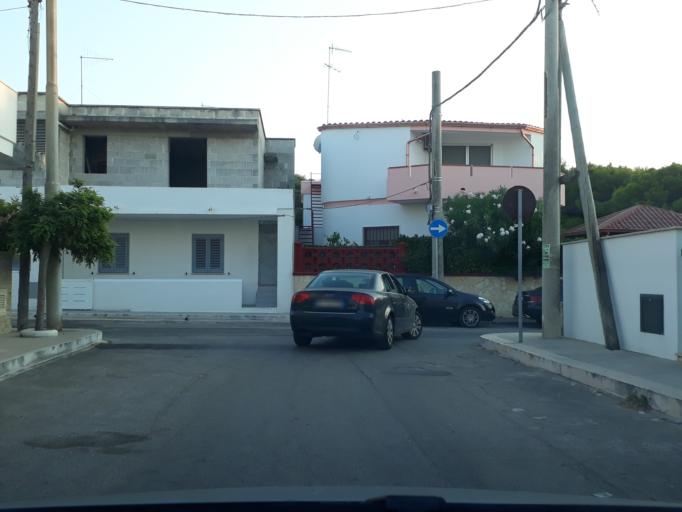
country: IT
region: Apulia
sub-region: Provincia di Brindisi
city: Carovigno
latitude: 40.7572
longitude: 17.7008
